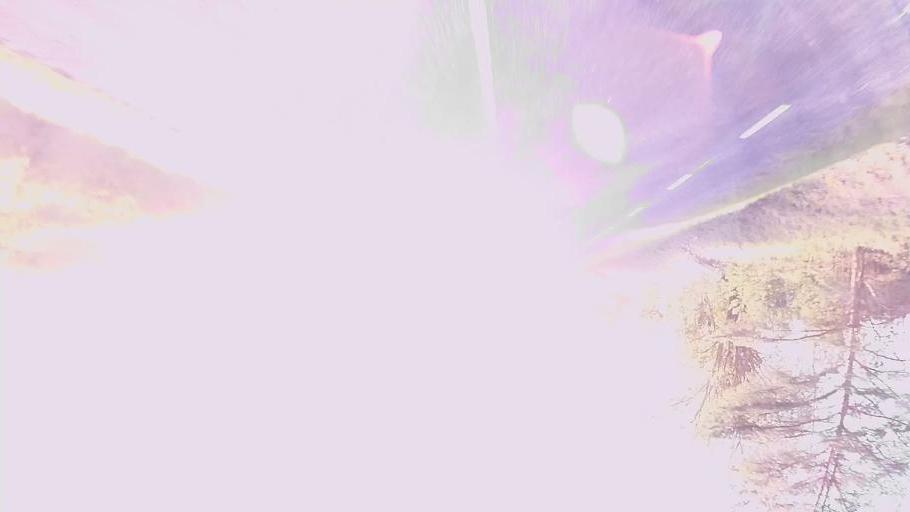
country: EE
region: Jogevamaa
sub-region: Poltsamaa linn
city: Poltsamaa
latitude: 58.5217
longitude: 25.9747
